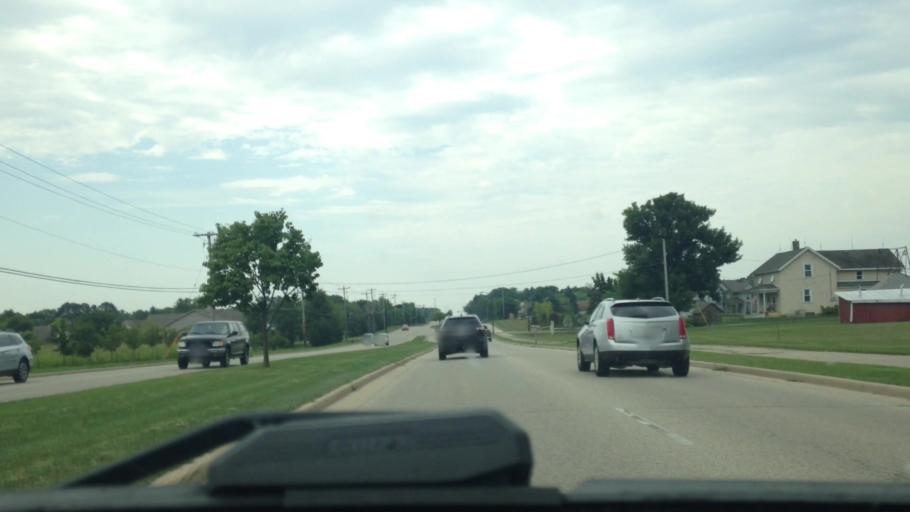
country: US
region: Wisconsin
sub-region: Waukesha County
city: Menomonee Falls
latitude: 43.1398
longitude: -88.1047
